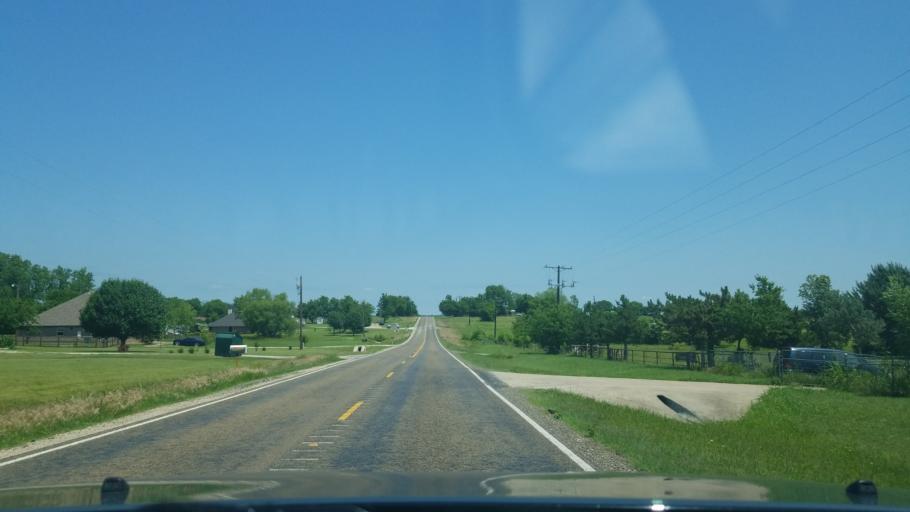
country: US
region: Texas
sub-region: Denton County
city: Sanger
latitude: 33.3334
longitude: -97.2386
